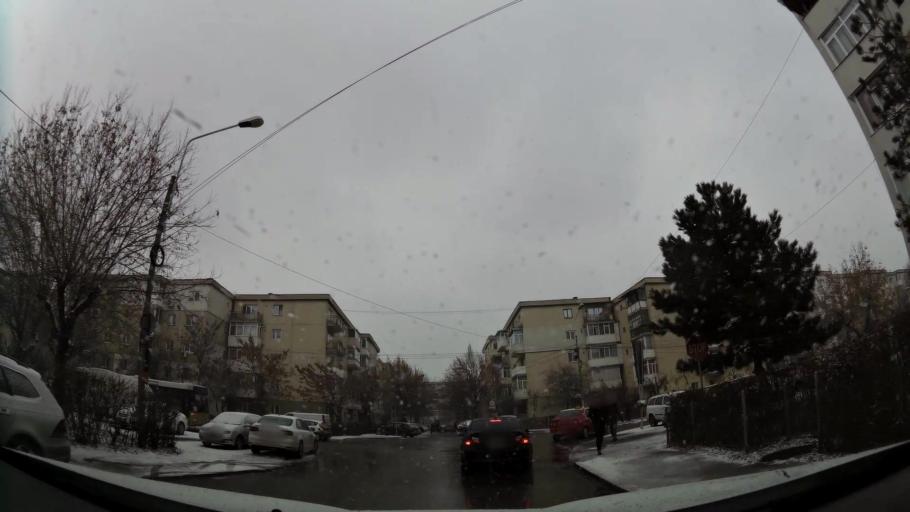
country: RO
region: Prahova
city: Ploiesti
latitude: 44.9299
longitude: 26.0029
